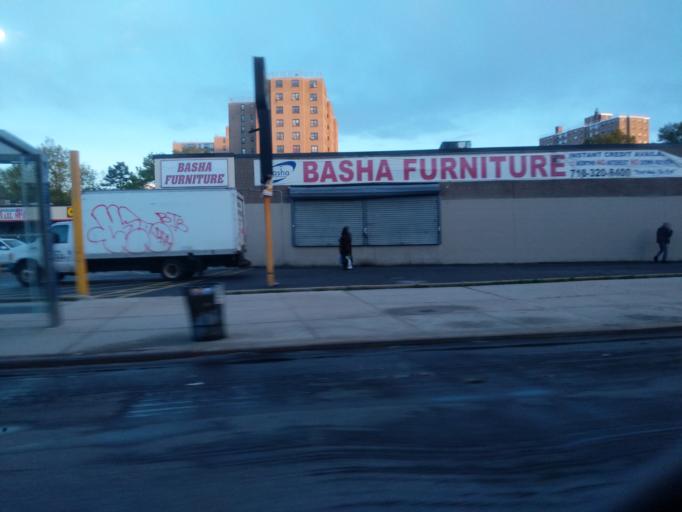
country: US
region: New York
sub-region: Bronx
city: Eastchester
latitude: 40.8843
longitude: -73.8332
